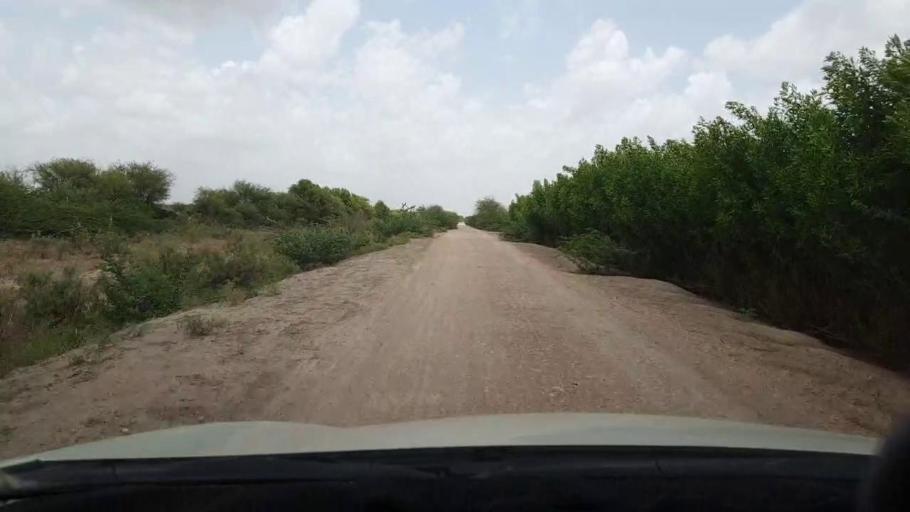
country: PK
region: Sindh
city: Kadhan
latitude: 24.3603
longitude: 68.9519
